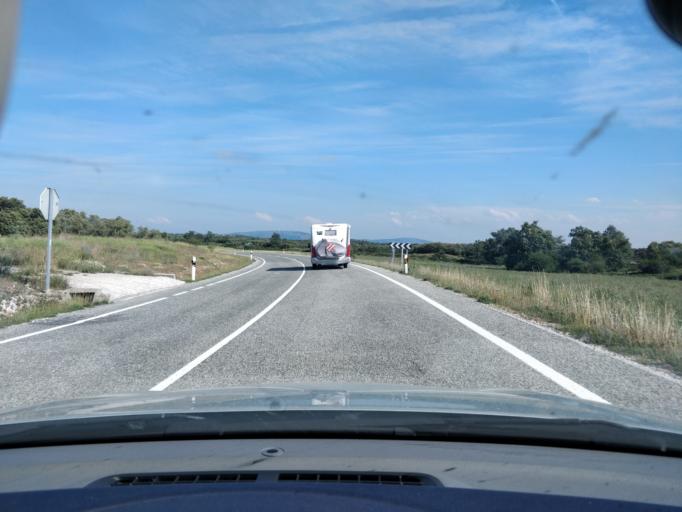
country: ES
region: Cantabria
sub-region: Provincia de Cantabria
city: San Martin de Elines
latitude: 42.9454
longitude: -3.7516
